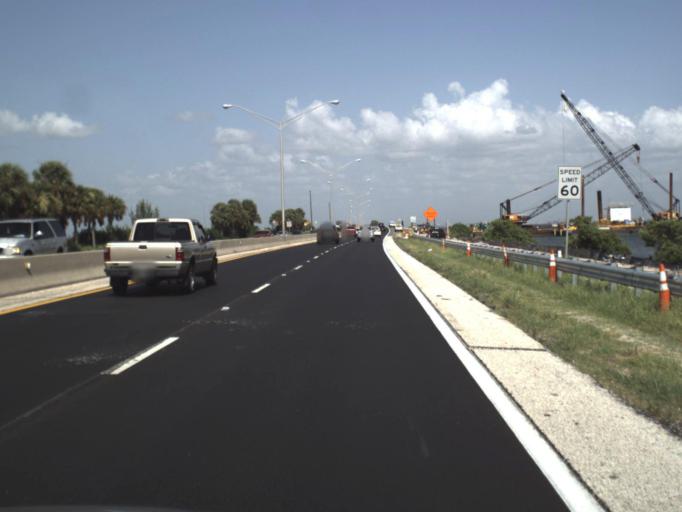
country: US
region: Florida
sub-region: Pinellas County
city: Safety Harbor
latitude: 27.9629
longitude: -82.6827
